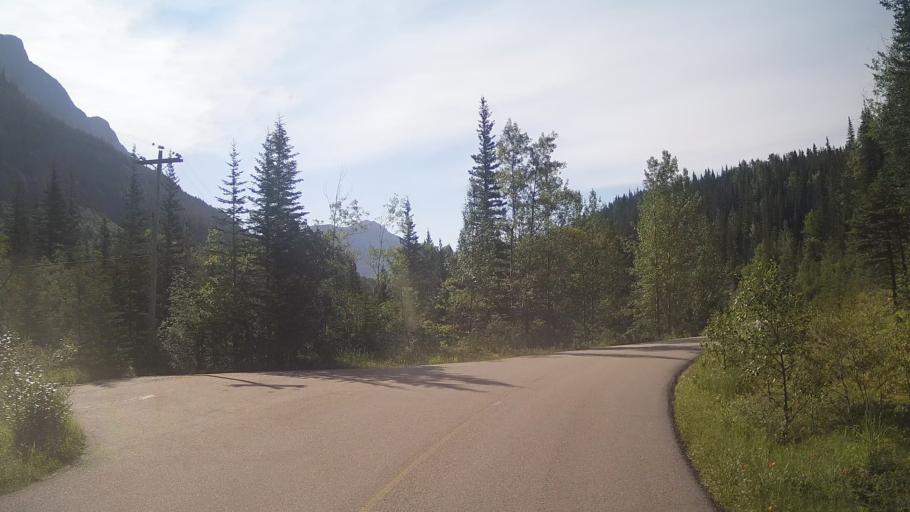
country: CA
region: Alberta
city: Hinton
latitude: 53.1742
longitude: -117.8283
